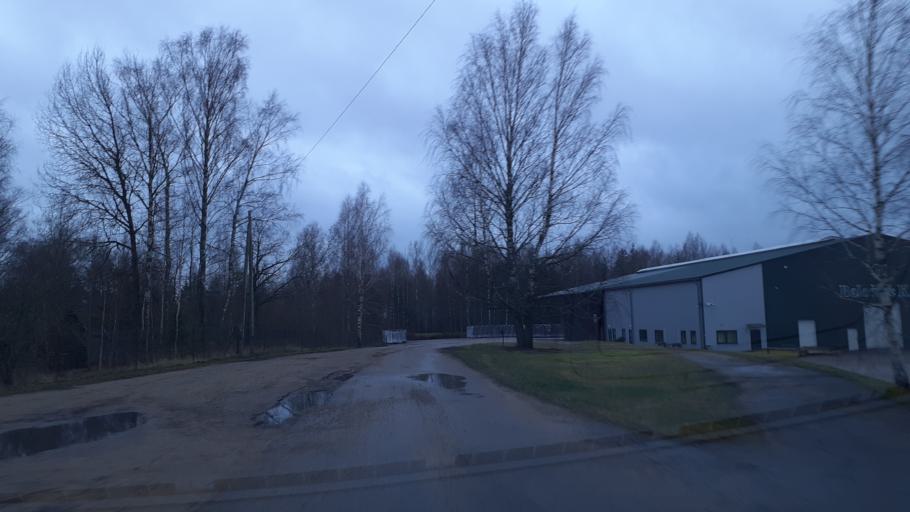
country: LV
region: Kuldigas Rajons
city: Kuldiga
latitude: 57.0389
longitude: 22.1268
